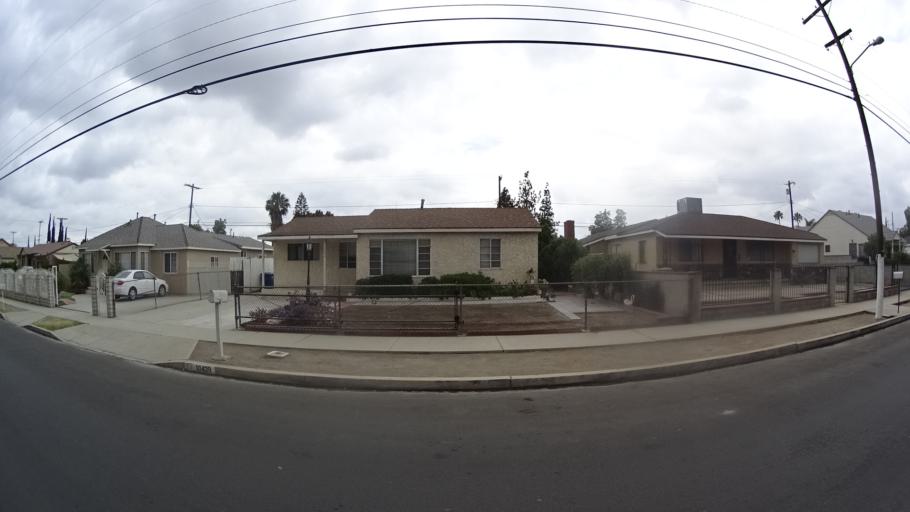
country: US
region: California
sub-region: Los Angeles County
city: San Fernando
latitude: 34.2603
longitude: -118.4395
